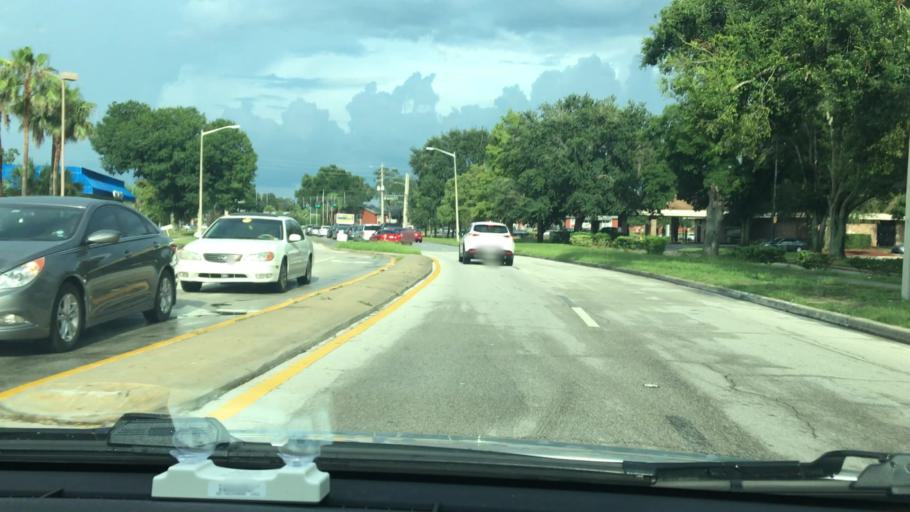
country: US
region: Florida
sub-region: Orange County
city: Conway
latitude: 28.5060
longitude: -81.3120
